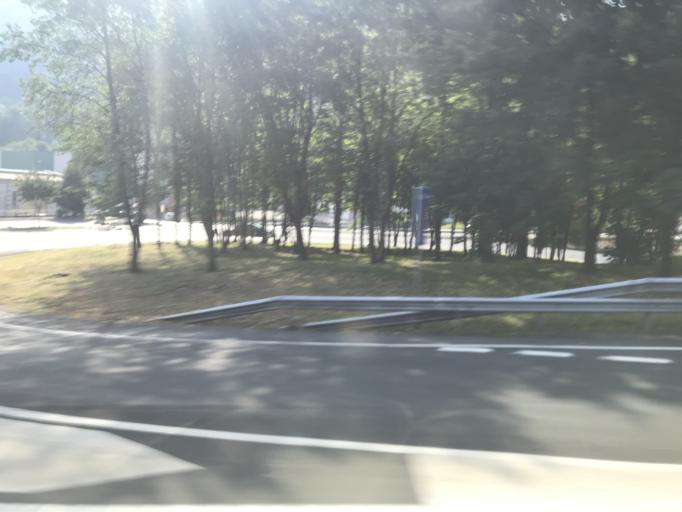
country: ES
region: Basque Country
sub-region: Provincia de Guipuzcoa
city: Irura
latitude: 43.1684
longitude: -2.0660
